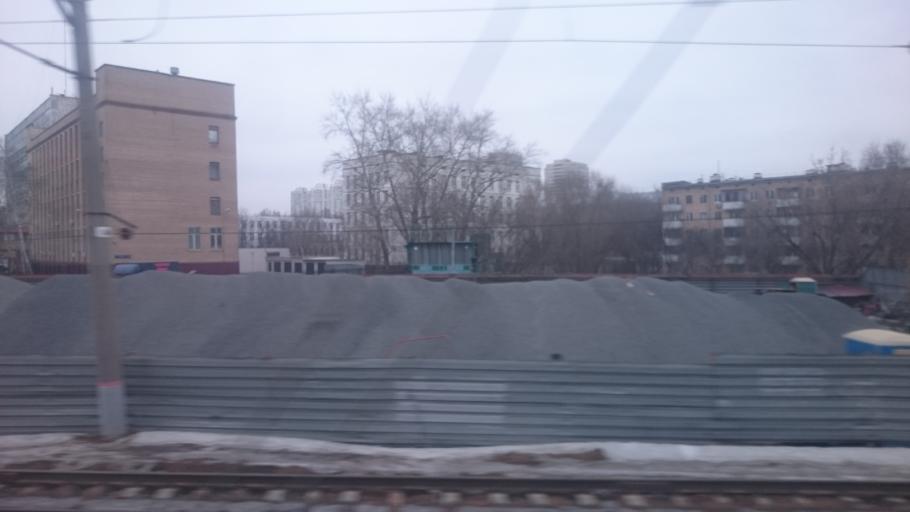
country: RU
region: Moscow
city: Pokrovskoye-Streshnevo
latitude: 55.8242
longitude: 37.4476
